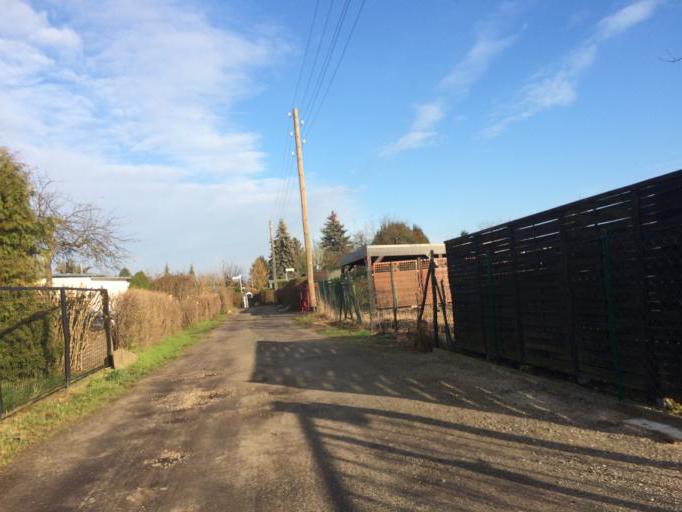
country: DE
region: Berlin
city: Heinersdorf
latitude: 52.5836
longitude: 13.4388
